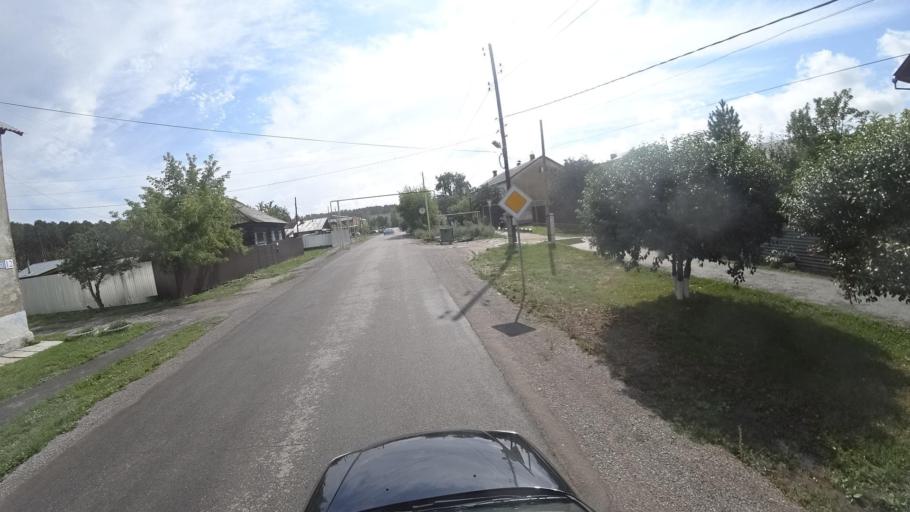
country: RU
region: Sverdlovsk
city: Kamyshlov
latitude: 56.8379
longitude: 62.7359
